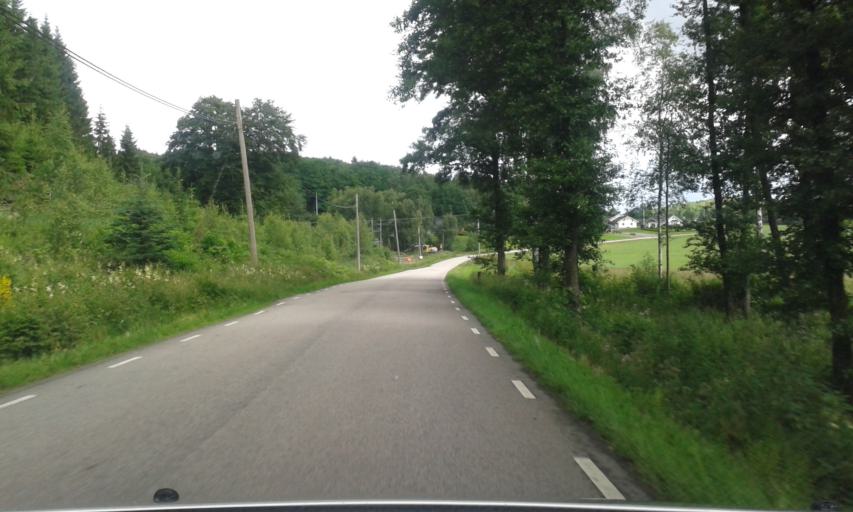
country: SE
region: Vaestra Goetaland
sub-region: Kungalvs Kommun
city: Kode
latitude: 57.9394
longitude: 11.8889
